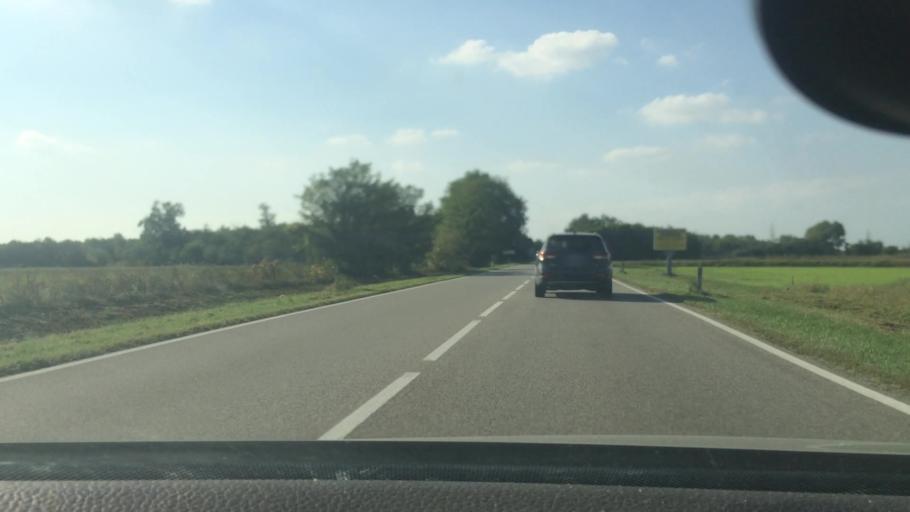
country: IT
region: Lombardy
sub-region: Citta metropolitana di Milano
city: Inveruno
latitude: 45.5260
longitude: 8.8468
